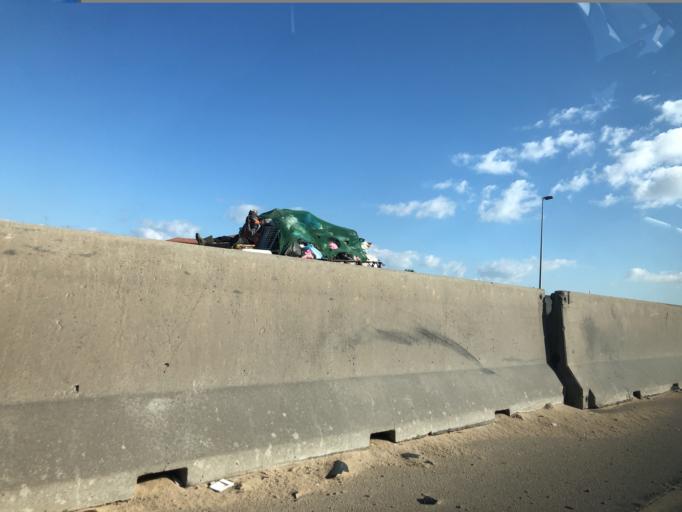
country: LY
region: Tripoli
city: Tripoli
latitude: 32.8562
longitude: 13.1985
